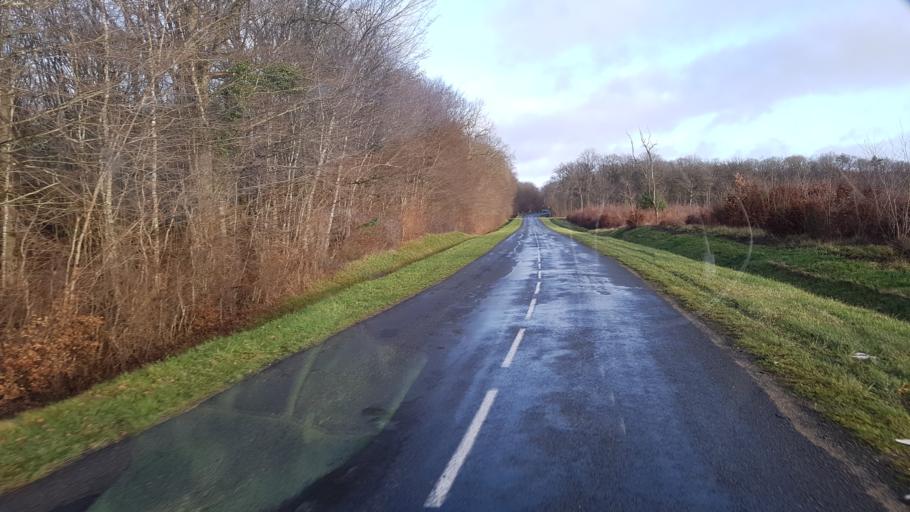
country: FR
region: Centre
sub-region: Departement du Loiret
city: Chilleurs-aux-Bois
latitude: 48.0193
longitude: 2.2063
